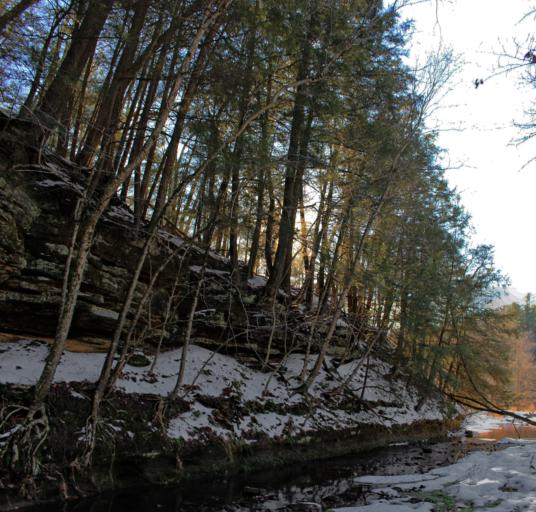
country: US
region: Wisconsin
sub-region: Sauk County
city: Reedsburg
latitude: 43.3622
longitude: -89.9819
